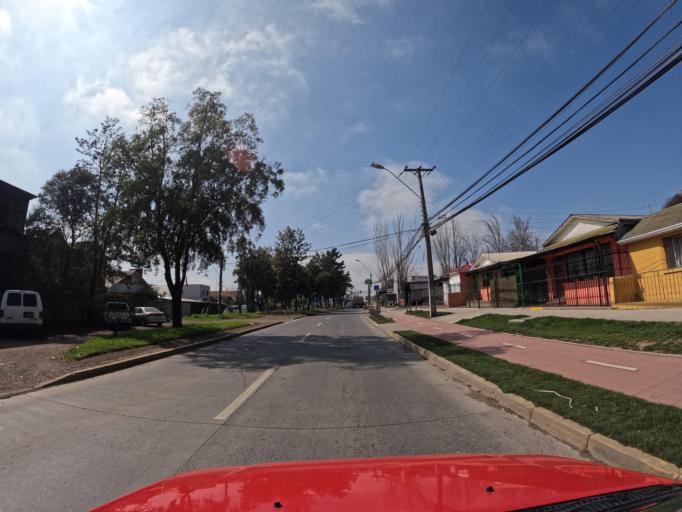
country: CL
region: Maule
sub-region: Provincia de Curico
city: Curico
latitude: -34.9758
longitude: -71.2238
